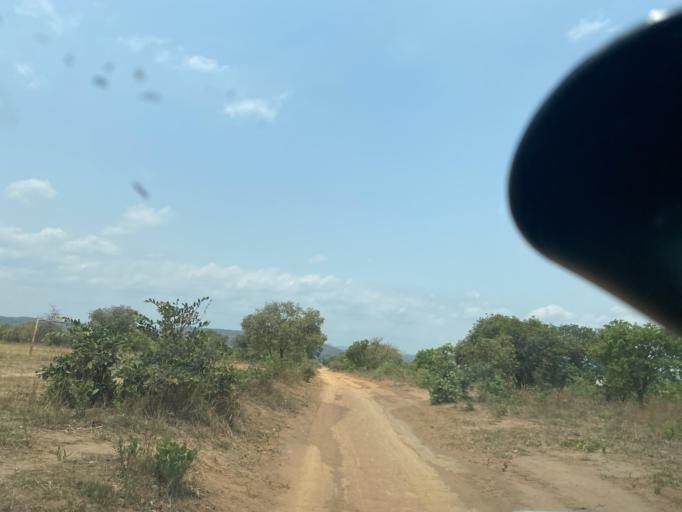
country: ZM
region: Lusaka
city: Chongwe
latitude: -15.5167
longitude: 28.8776
